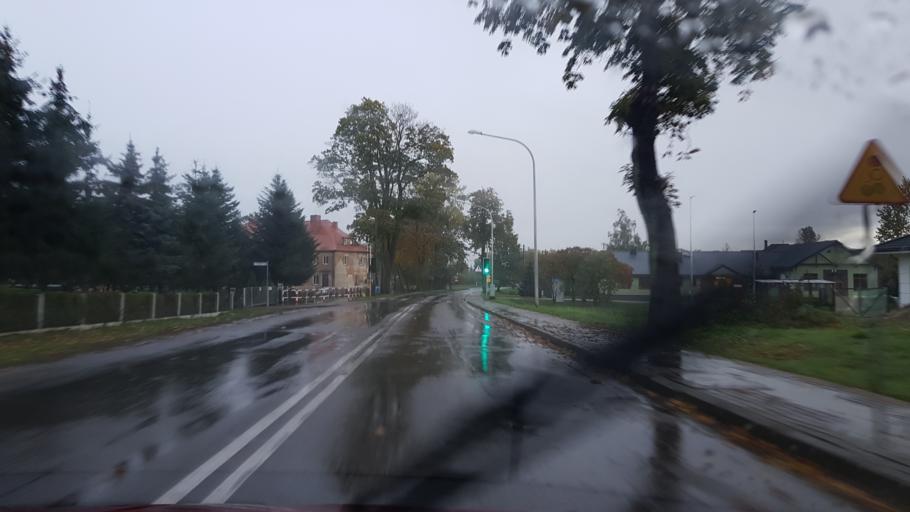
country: PL
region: Greater Poland Voivodeship
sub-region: Powiat pilski
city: Szydlowo
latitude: 53.1637
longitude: 16.6087
